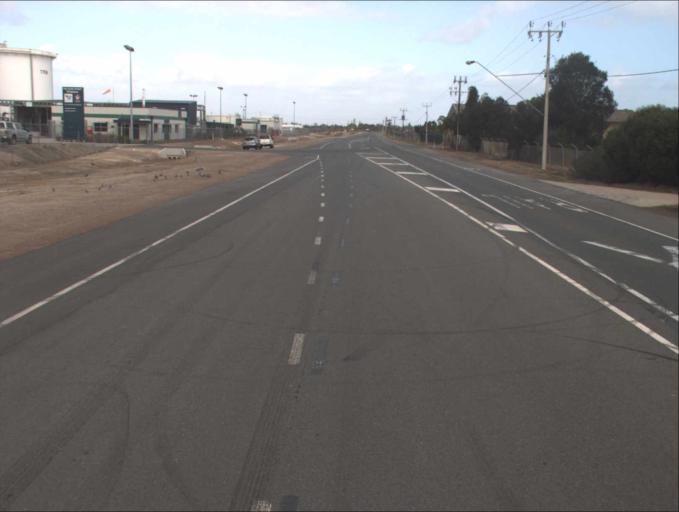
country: AU
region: South Australia
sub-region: Port Adelaide Enfield
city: Birkenhead
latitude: -34.7737
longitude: 138.5016
